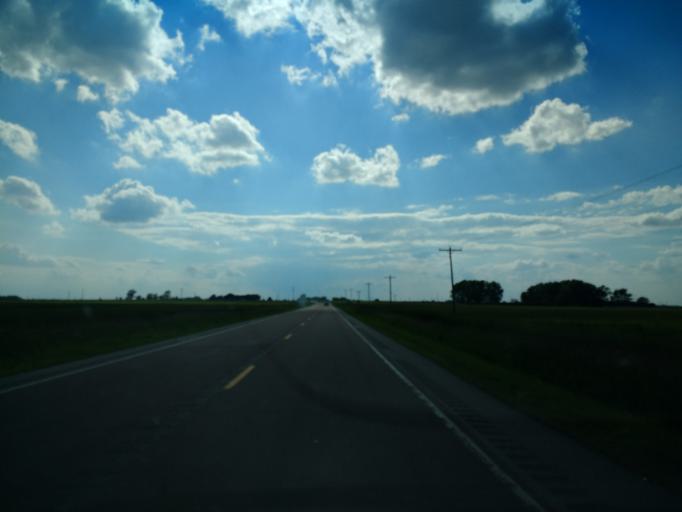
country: US
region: Iowa
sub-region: Clay County
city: Spencer
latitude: 43.1837
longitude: -95.2256
